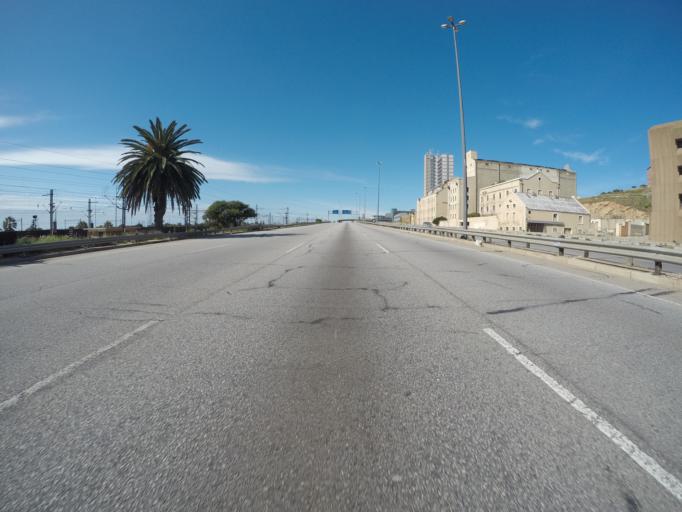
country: ZA
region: Eastern Cape
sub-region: Nelson Mandela Bay Metropolitan Municipality
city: Port Elizabeth
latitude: -33.9544
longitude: 25.6159
